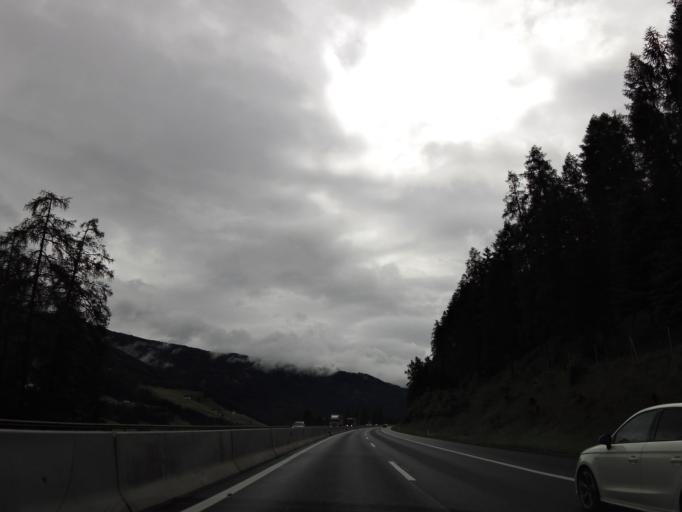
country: AT
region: Tyrol
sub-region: Politischer Bezirk Innsbruck Land
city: Ellbogen
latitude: 47.1586
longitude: 11.4382
